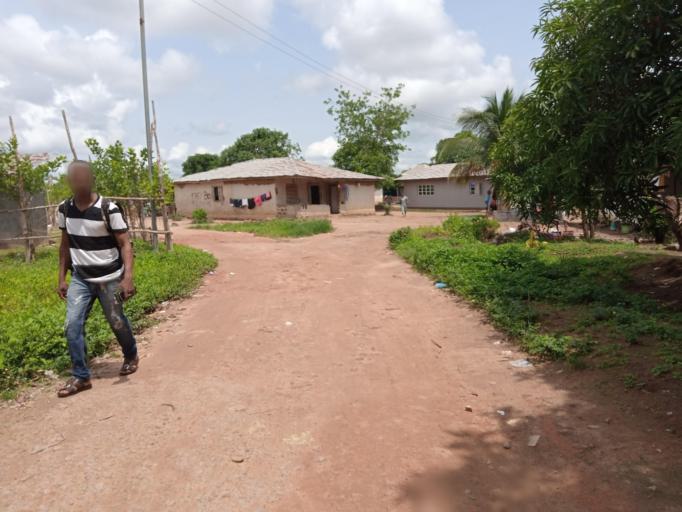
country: SL
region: Southern Province
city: Bo
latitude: 7.9415
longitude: -11.7216
